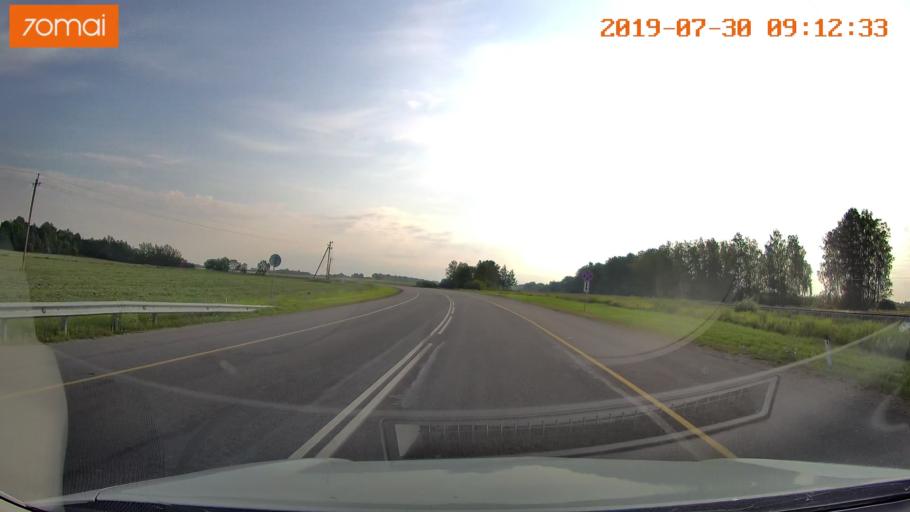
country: RU
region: Kaliningrad
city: Nesterov
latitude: 54.6171
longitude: 22.4777
